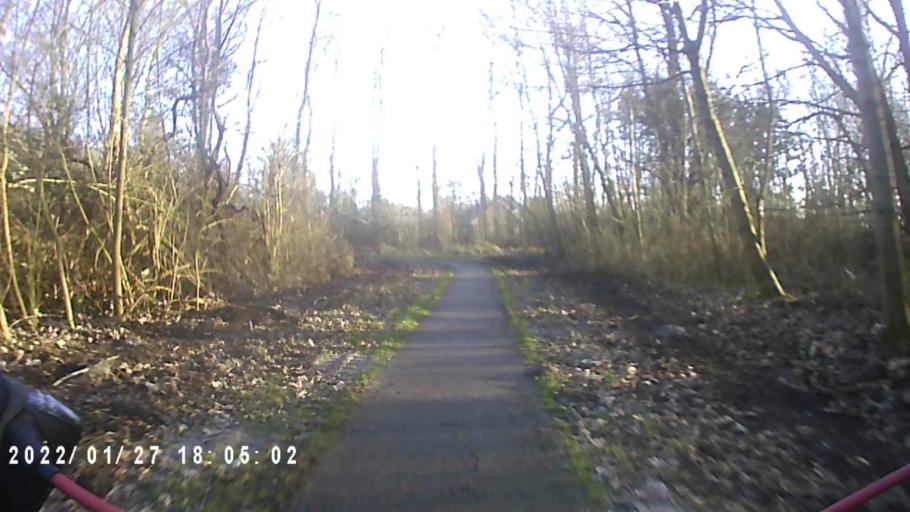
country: NL
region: Friesland
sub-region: Gemeente Dongeradeel
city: Anjum
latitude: 53.4063
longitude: 6.2170
